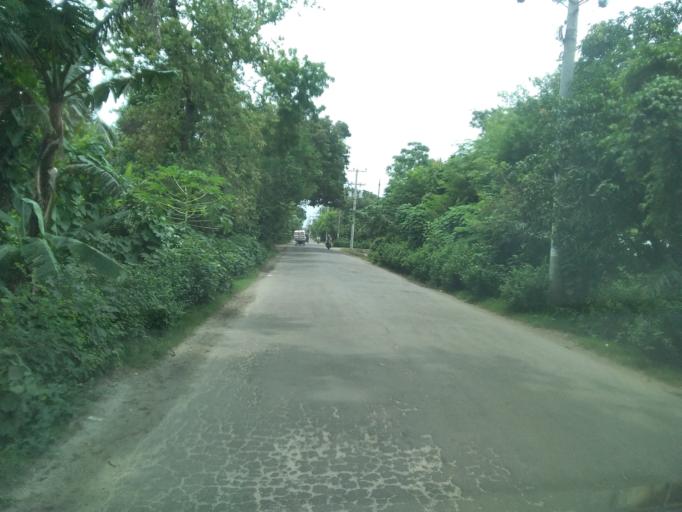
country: IN
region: West Bengal
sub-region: North 24 Parganas
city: Taki
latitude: 22.5745
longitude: 88.9996
